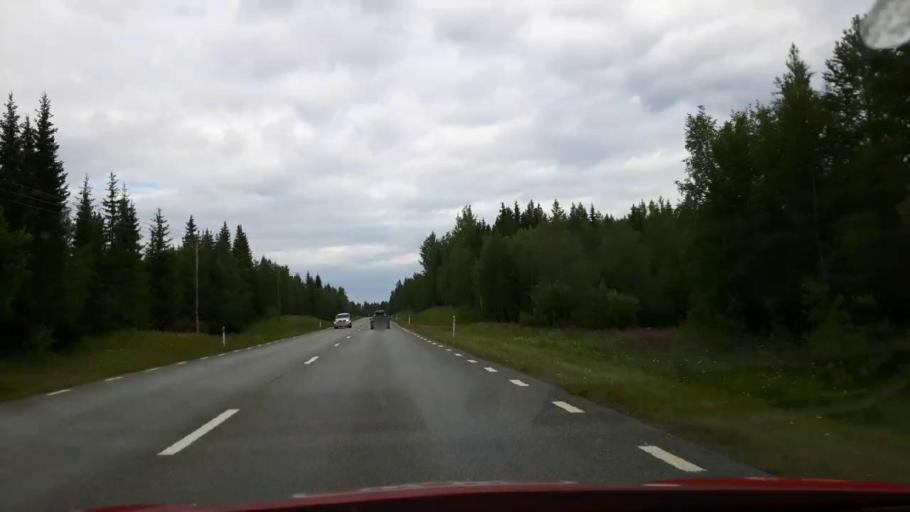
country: SE
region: Jaemtland
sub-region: Stroemsunds Kommun
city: Stroemsund
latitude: 63.6255
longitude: 15.3556
